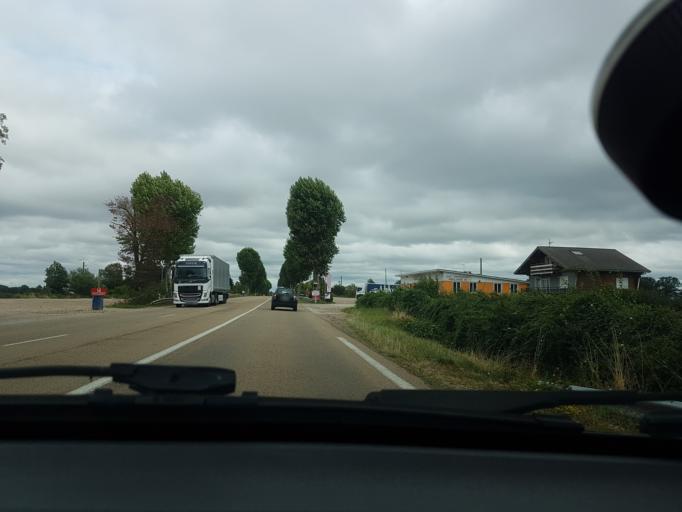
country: FR
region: Bourgogne
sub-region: Departement de l'Yonne
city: Avallon
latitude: 47.4790
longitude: 4.0075
